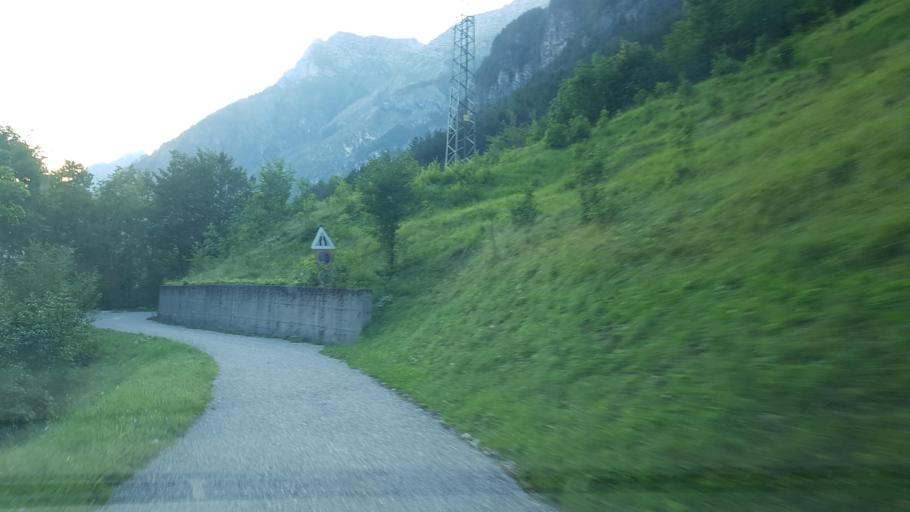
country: IT
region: Friuli Venezia Giulia
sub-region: Provincia di Udine
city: Malborghetto
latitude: 46.3969
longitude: 13.4387
